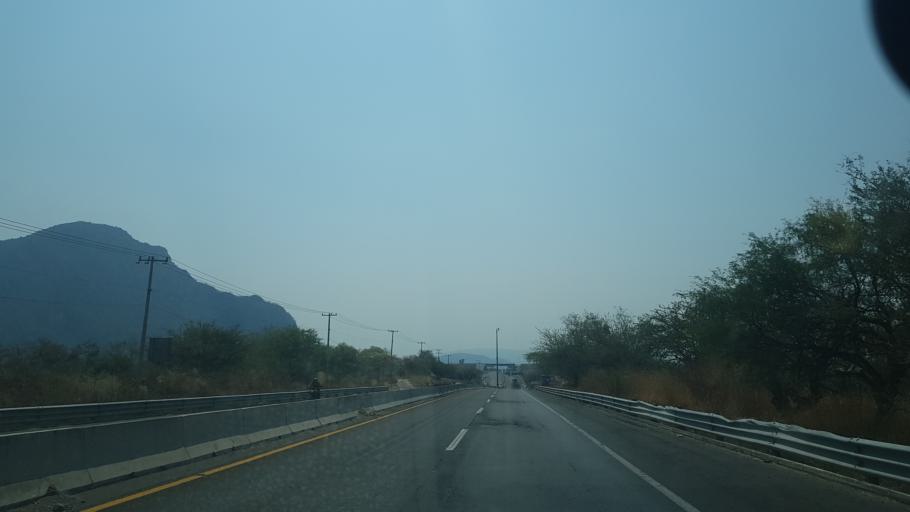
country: MX
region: Morelos
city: Jantetelco
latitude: 18.7069
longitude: -98.7751
